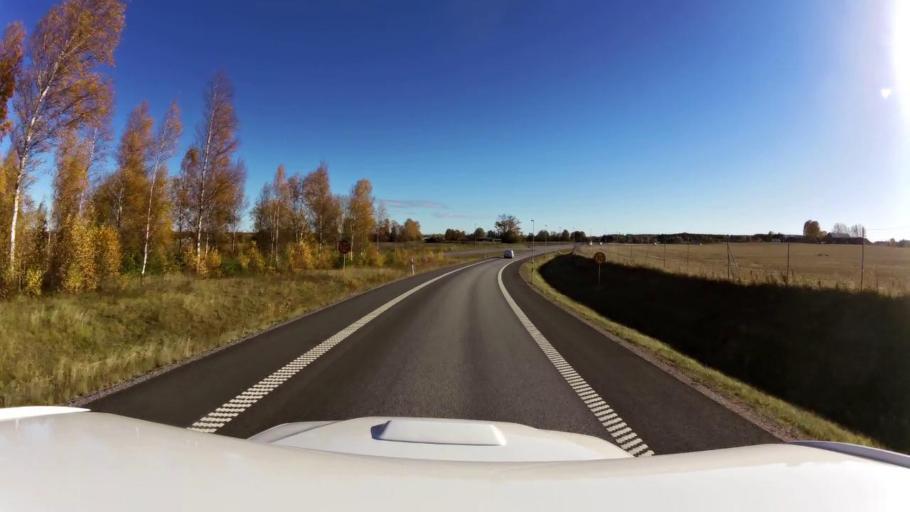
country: SE
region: OEstergoetland
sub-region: Linkopings Kommun
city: Malmslatt
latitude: 58.4336
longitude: 15.5266
